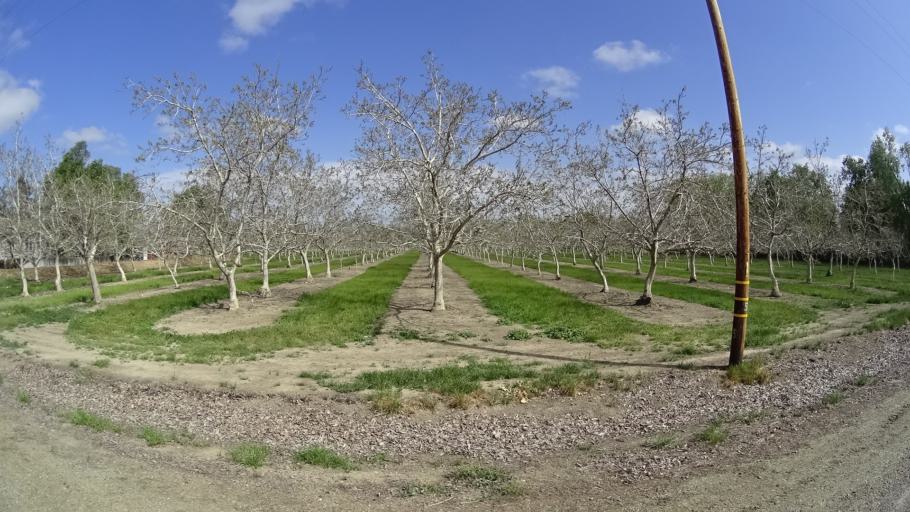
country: US
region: California
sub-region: Colusa County
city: Colusa
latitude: 39.4200
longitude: -121.9628
